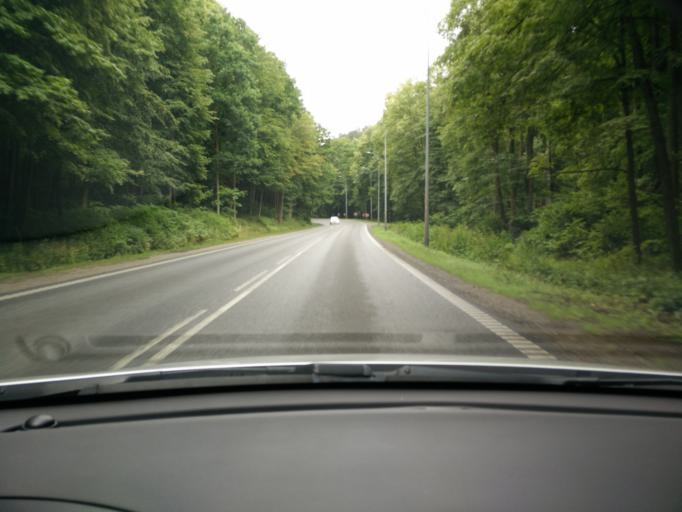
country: PL
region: Pomeranian Voivodeship
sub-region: Sopot
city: Sopot
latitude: 54.4216
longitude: 18.5149
